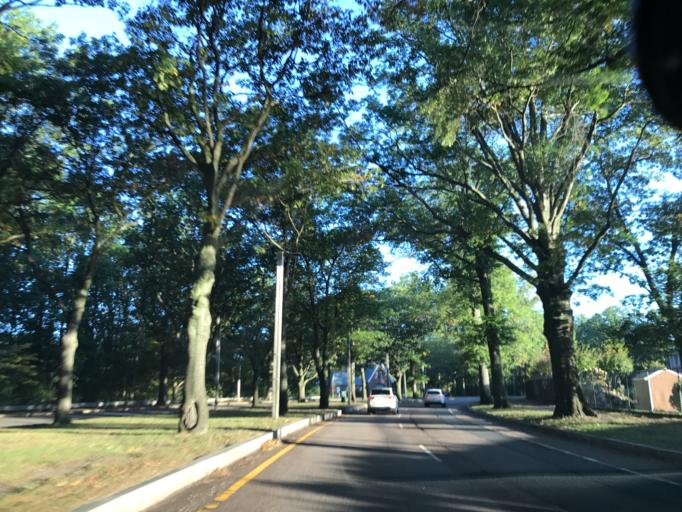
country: US
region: Massachusetts
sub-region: Norfolk County
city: Dedham
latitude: 42.2726
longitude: -71.1735
